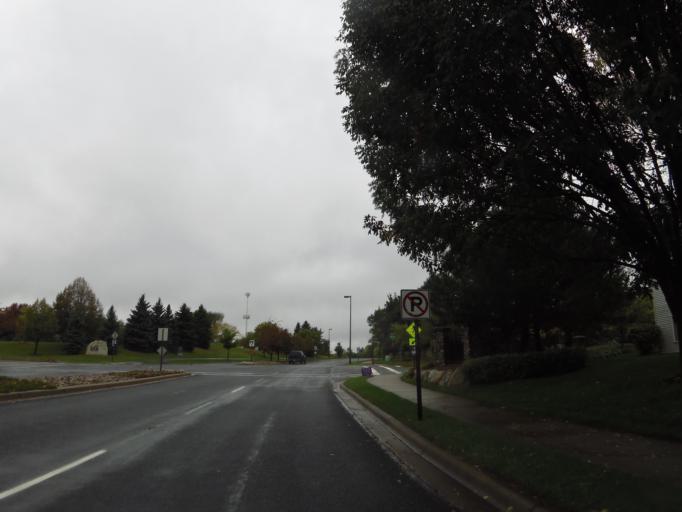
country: US
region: Minnesota
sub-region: Dakota County
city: Inver Grove Heights
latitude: 44.8242
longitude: -93.0421
